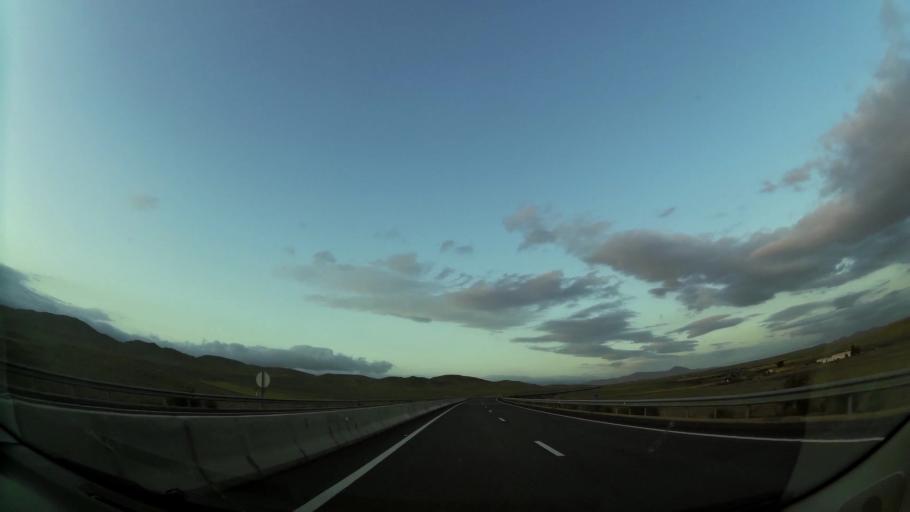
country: MA
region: Oriental
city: Taourirt
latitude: 34.5830
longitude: -2.8049
